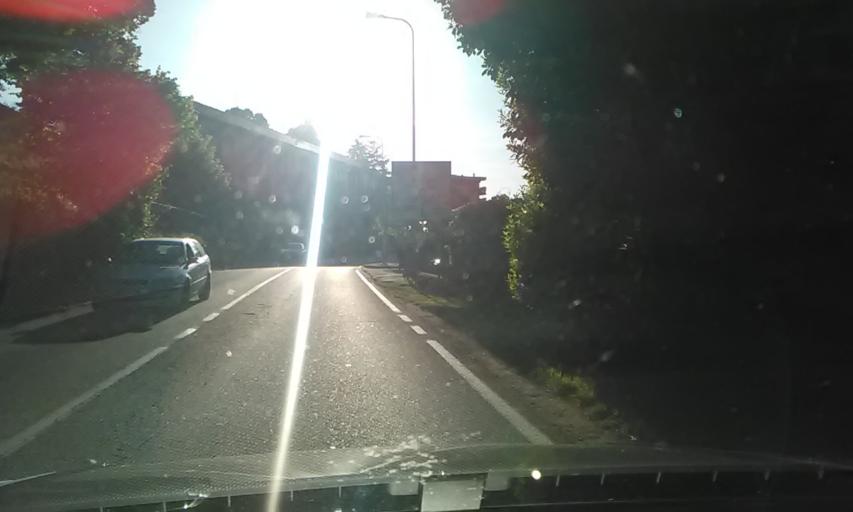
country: IT
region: Piedmont
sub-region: Provincia di Novara
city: Oleggio
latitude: 45.5949
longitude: 8.6361
